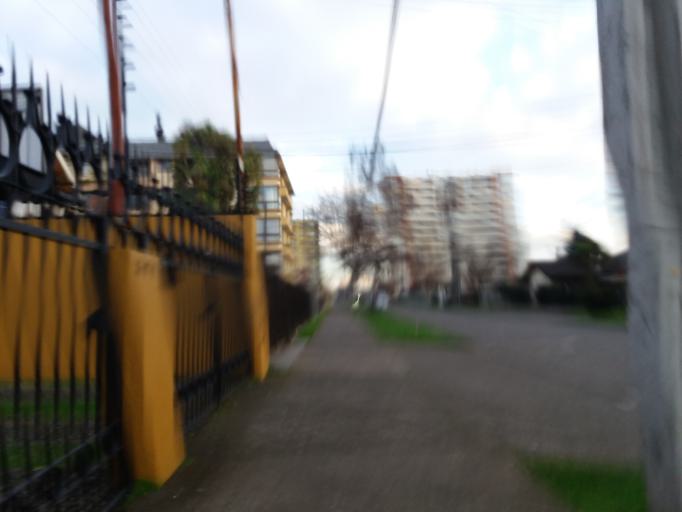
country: CL
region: Araucania
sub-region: Provincia de Cautin
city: Temuco
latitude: -38.7370
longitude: -72.6044
